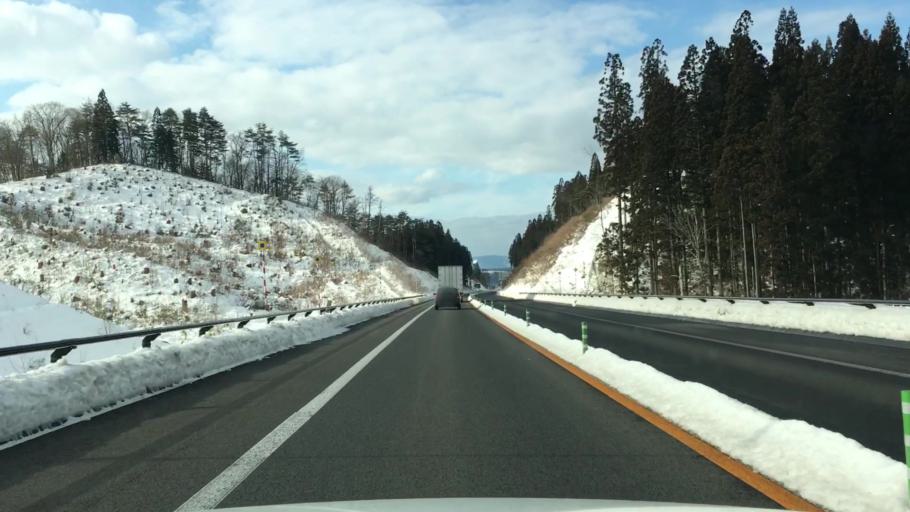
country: JP
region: Akita
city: Takanosu
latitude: 40.2103
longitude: 140.4142
